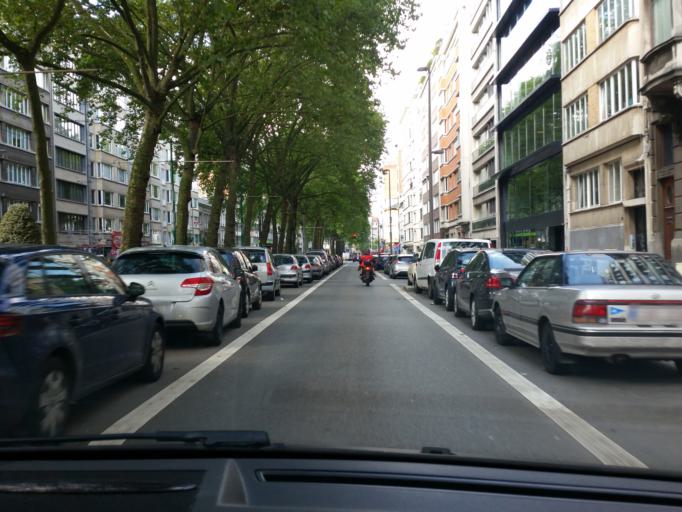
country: BE
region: Flanders
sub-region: Provincie Antwerpen
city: Antwerpen
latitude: 51.2028
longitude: 4.4122
